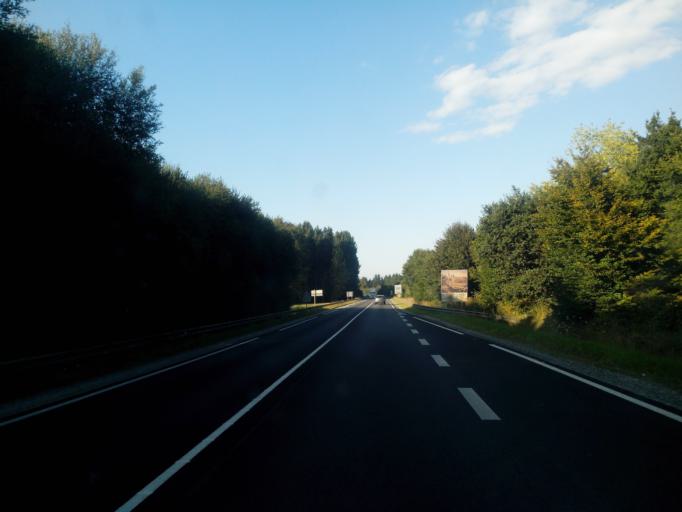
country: FR
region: Brittany
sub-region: Departement du Morbihan
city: Saint-Thuriau
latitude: 48.0433
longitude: -2.9484
